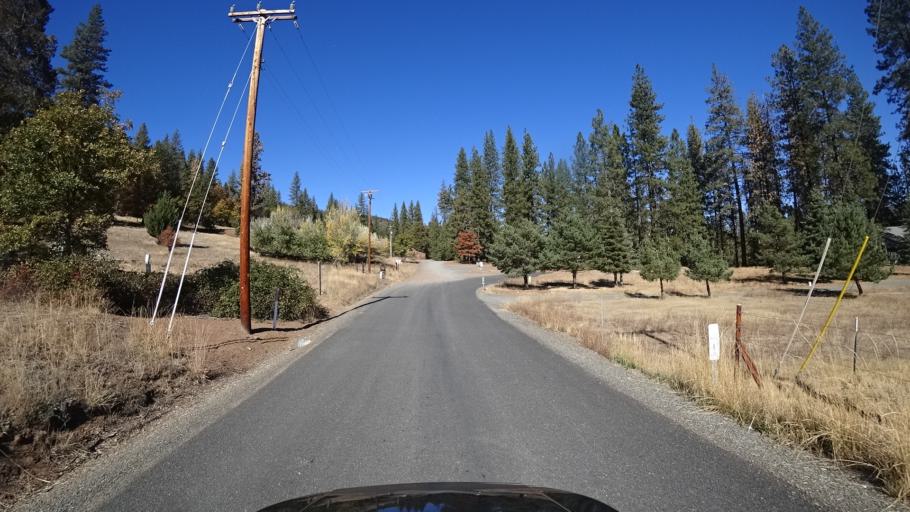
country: US
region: California
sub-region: Siskiyou County
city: Yreka
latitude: 41.5800
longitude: -122.9211
